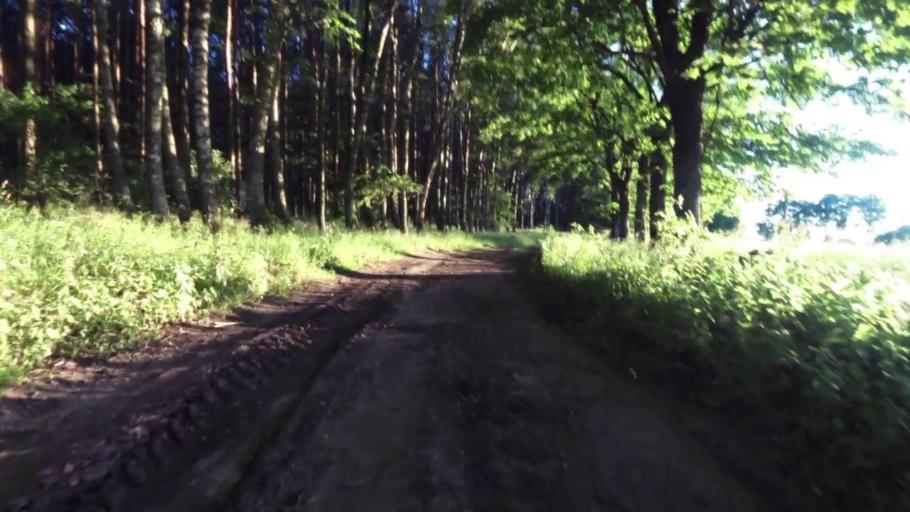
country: PL
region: West Pomeranian Voivodeship
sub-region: Powiat bialogardzki
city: Bialogard
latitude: 54.0560
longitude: 16.0998
